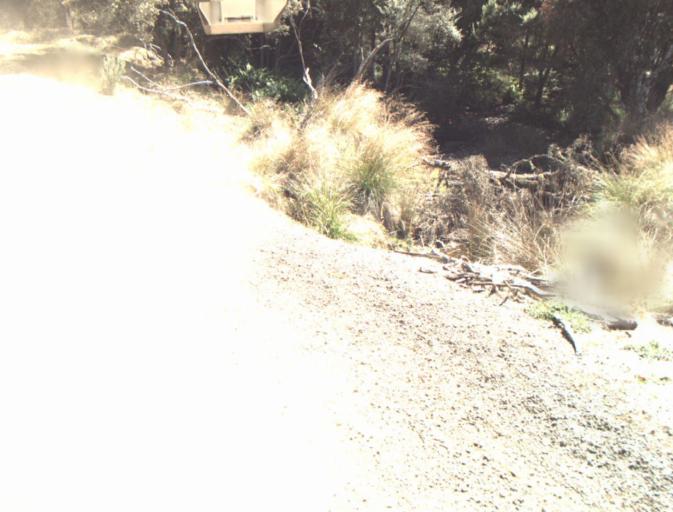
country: AU
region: Tasmania
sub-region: Dorset
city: Scottsdale
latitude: -41.2882
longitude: 147.3407
